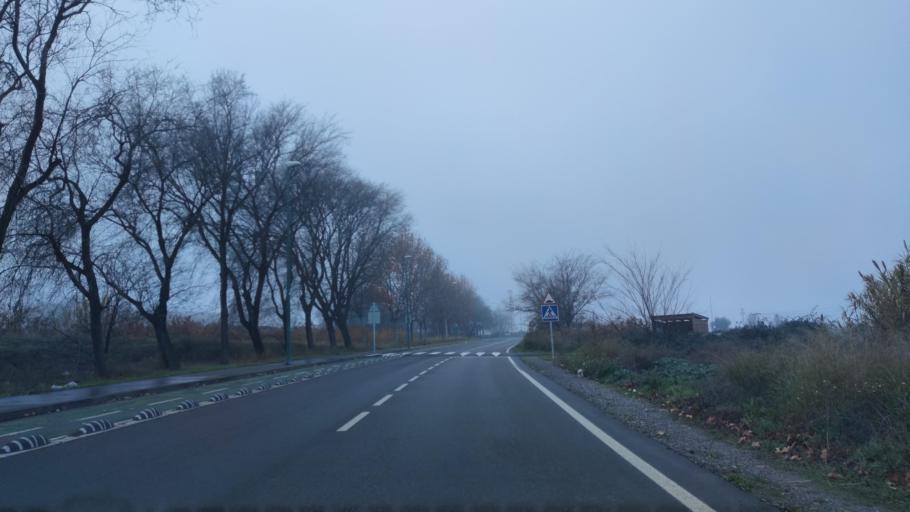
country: ES
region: Aragon
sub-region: Provincia de Zaragoza
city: Utebo
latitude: 41.7139
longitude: -1.0120
